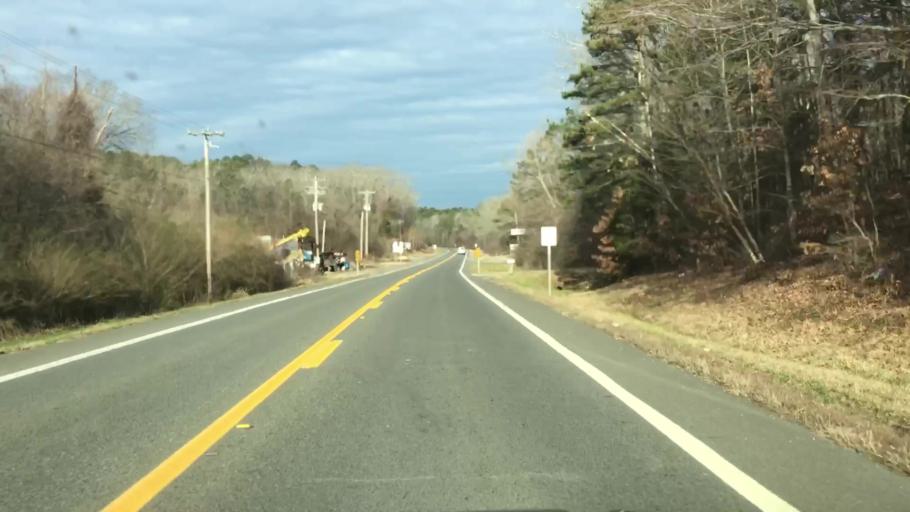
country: US
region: Arkansas
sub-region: Montgomery County
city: Mount Ida
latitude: 34.5628
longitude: -93.6407
